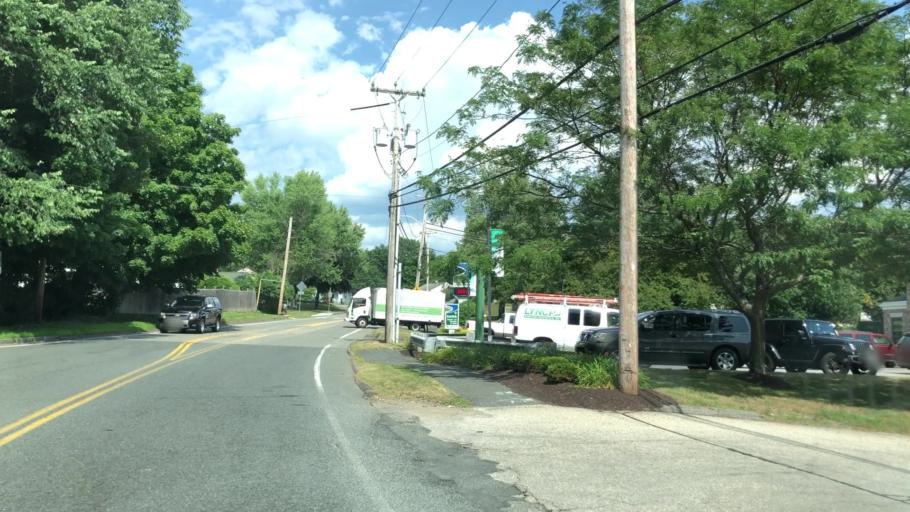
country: US
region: Massachusetts
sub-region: Hampden County
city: Holyoke
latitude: 42.1873
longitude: -72.6500
